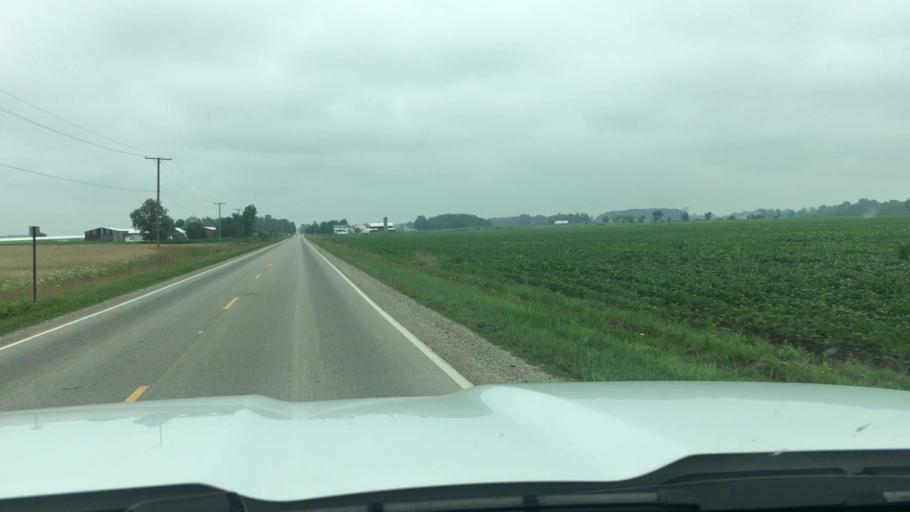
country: US
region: Michigan
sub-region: Sanilac County
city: Brown City
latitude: 43.2859
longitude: -82.9828
